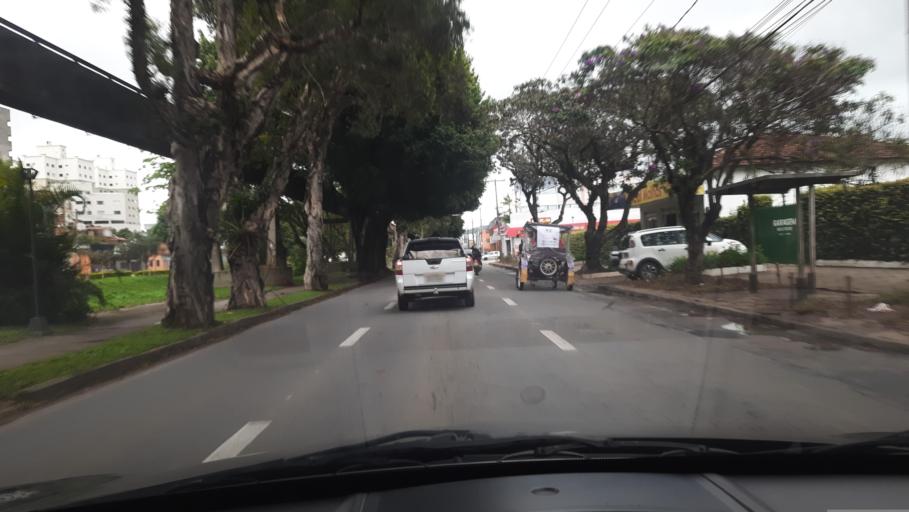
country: BR
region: Minas Gerais
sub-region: Pocos De Caldas
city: Pocos de Caldas
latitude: -21.7854
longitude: -46.5811
